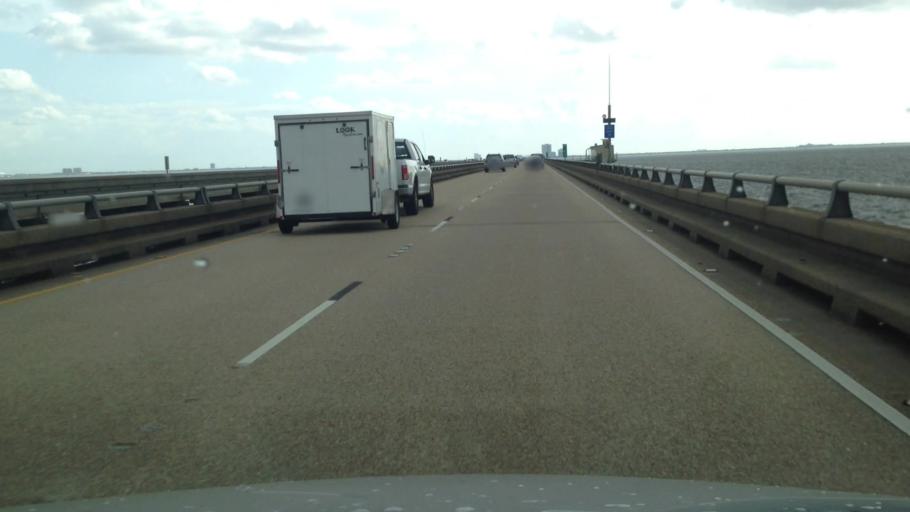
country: US
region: Louisiana
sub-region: Jefferson Parish
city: Metairie
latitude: 30.0917
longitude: -90.1419
